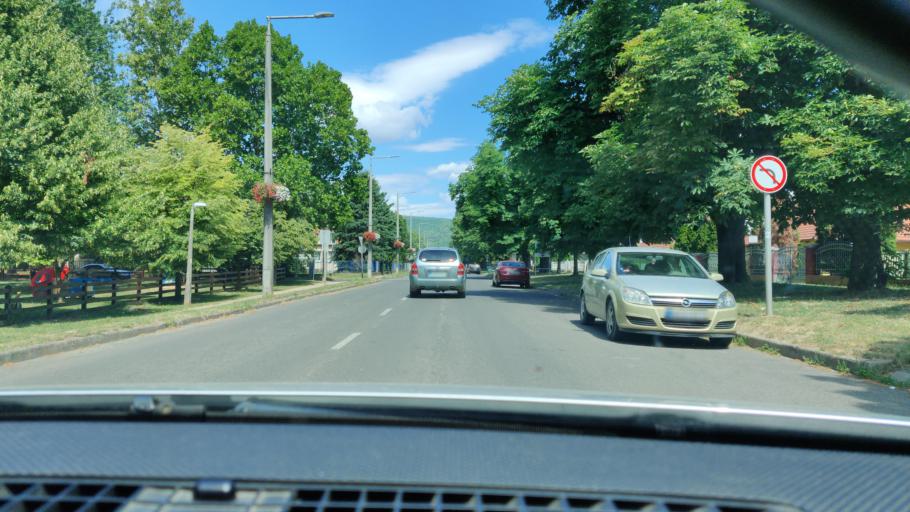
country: HU
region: Baranya
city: Siklos
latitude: 45.8599
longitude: 18.2894
